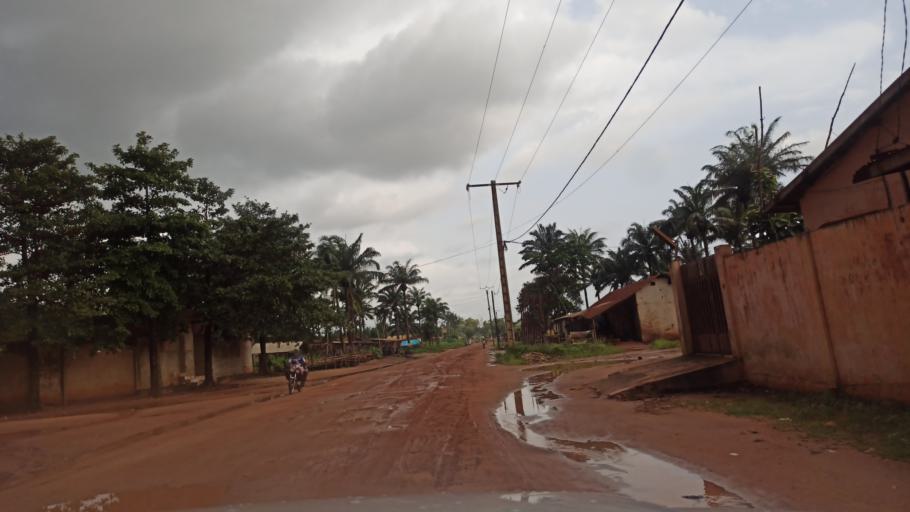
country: BJ
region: Queme
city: Porto-Novo
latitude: 6.5586
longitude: 2.5919
